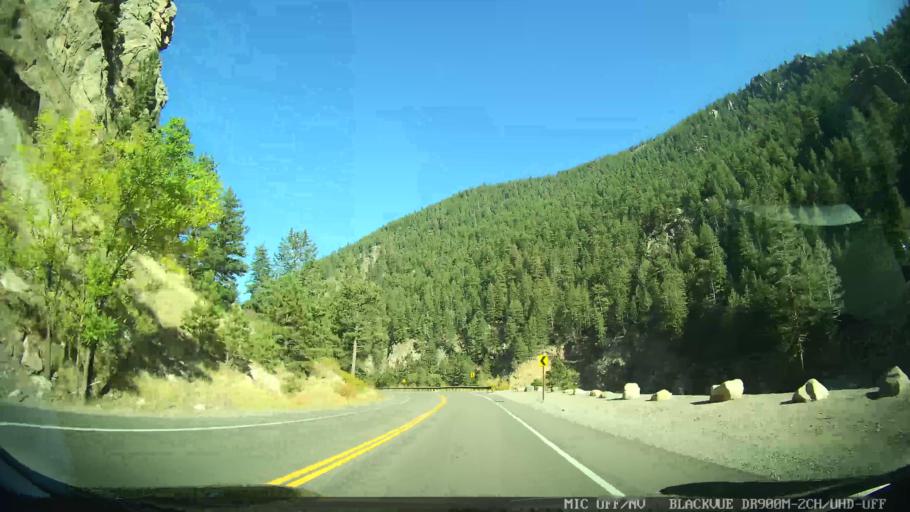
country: US
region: Colorado
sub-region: Larimer County
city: Estes Park
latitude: 40.4099
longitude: -105.3807
